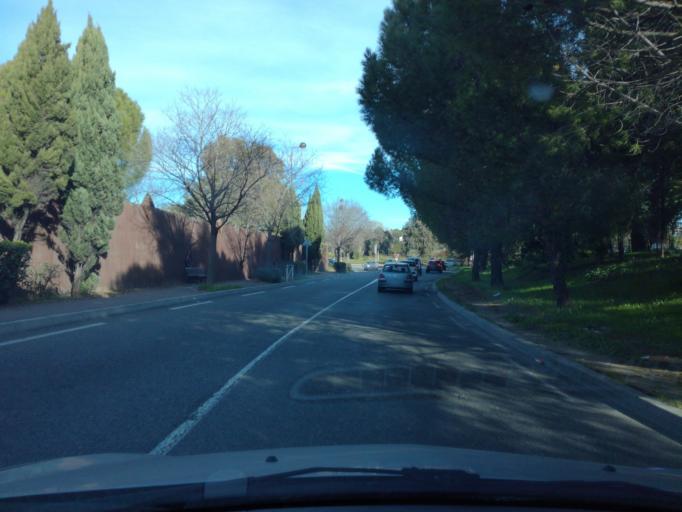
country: FR
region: Provence-Alpes-Cote d'Azur
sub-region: Departement des Alpes-Maritimes
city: Vallauris
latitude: 43.5772
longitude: 7.0903
